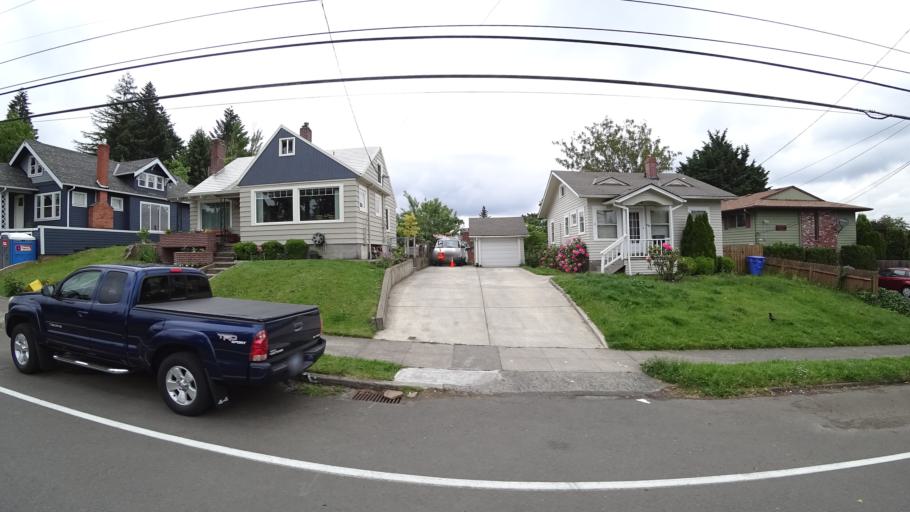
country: US
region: Oregon
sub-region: Multnomah County
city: Lents
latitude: 45.5027
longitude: -122.6091
